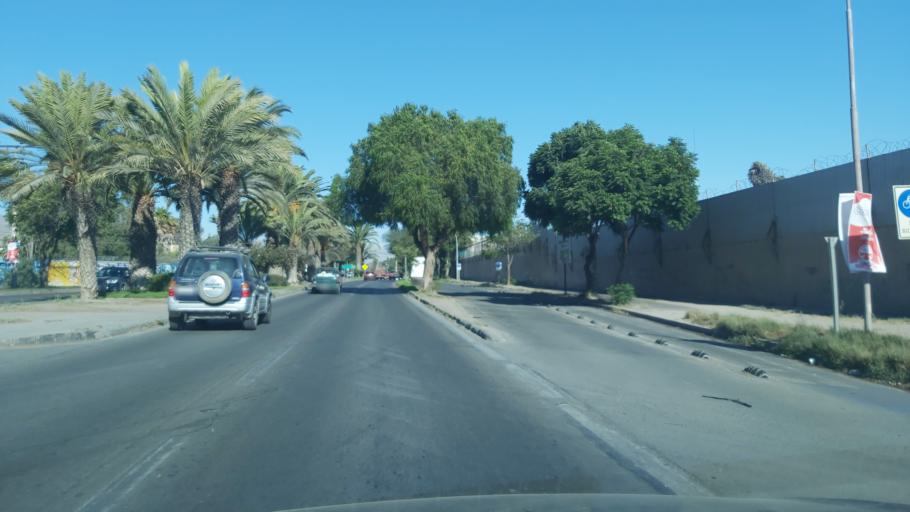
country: CL
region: Atacama
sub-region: Provincia de Copiapo
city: Copiapo
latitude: -27.3724
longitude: -70.3308
